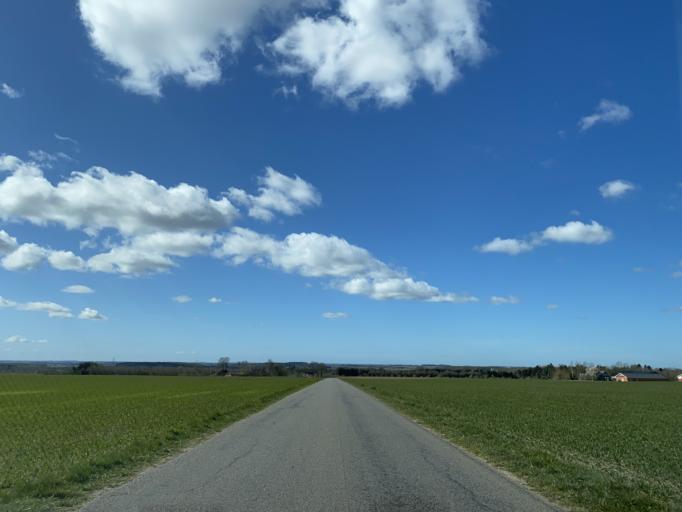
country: DK
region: Central Jutland
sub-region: Favrskov Kommune
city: Ulstrup
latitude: 56.3434
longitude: 9.8017
